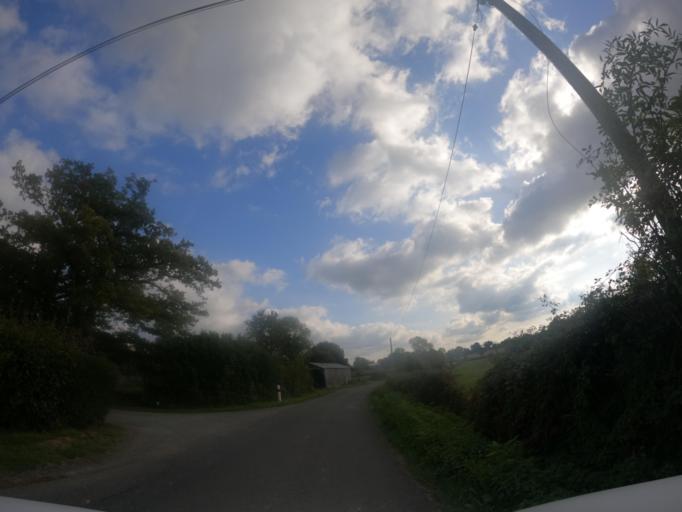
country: FR
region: Poitou-Charentes
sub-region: Departement des Deux-Sevres
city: La Foret-sur-Sevre
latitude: 46.7939
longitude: -0.6124
